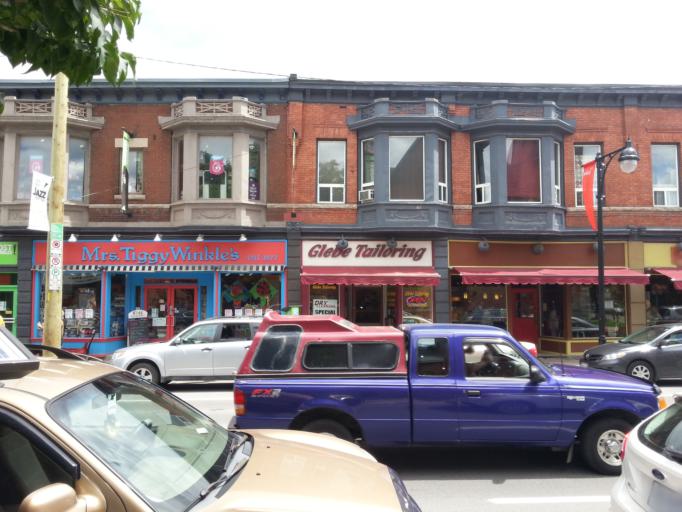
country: CA
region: Ontario
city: Ottawa
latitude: 45.4026
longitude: -75.6882
